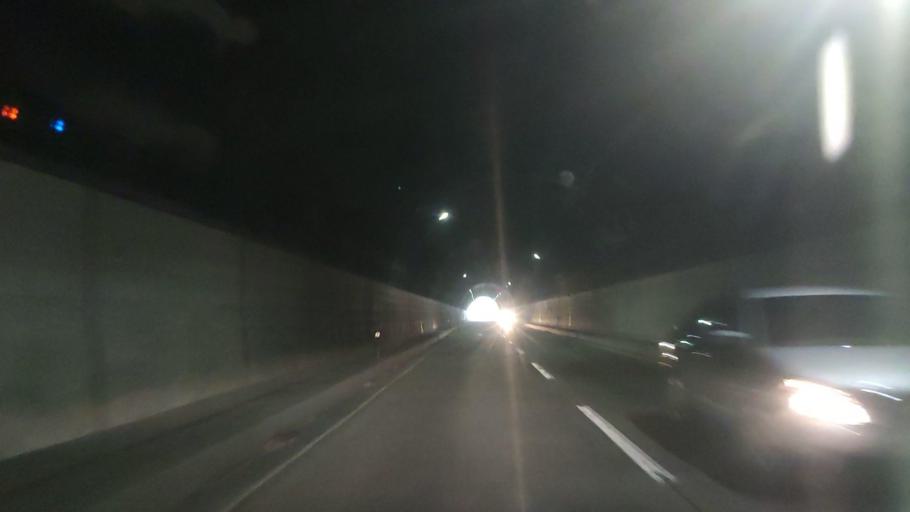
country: JP
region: Kagoshima
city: Okuchi-shinohara
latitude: 31.9733
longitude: 130.7409
